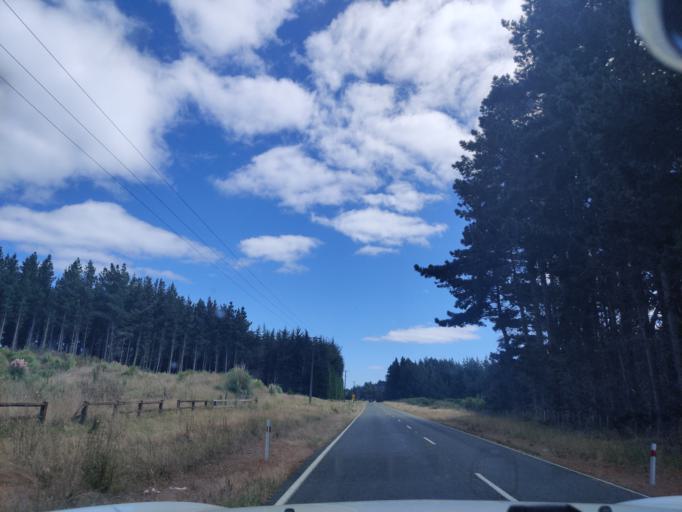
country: NZ
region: Manawatu-Wanganui
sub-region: Horowhenua District
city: Foxton
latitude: -40.3771
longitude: 175.2537
